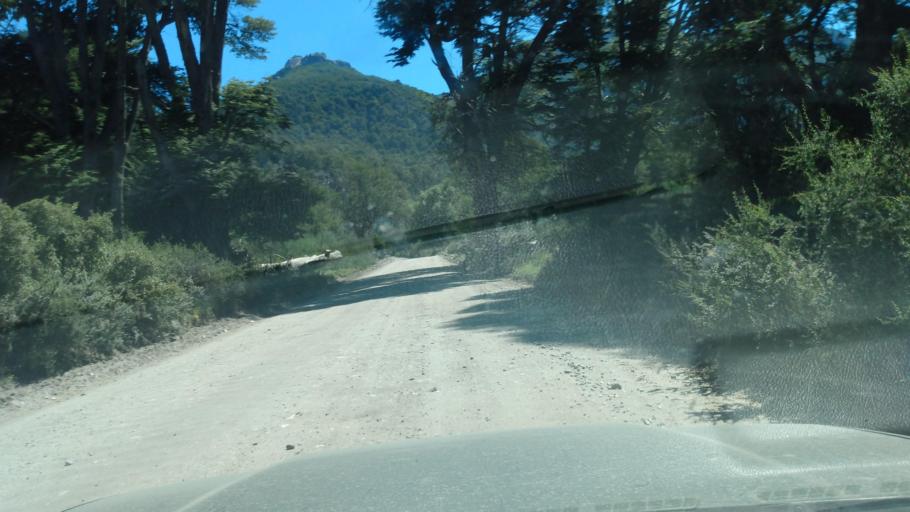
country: AR
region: Neuquen
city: Villa La Angostura
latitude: -40.6242
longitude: -71.5853
